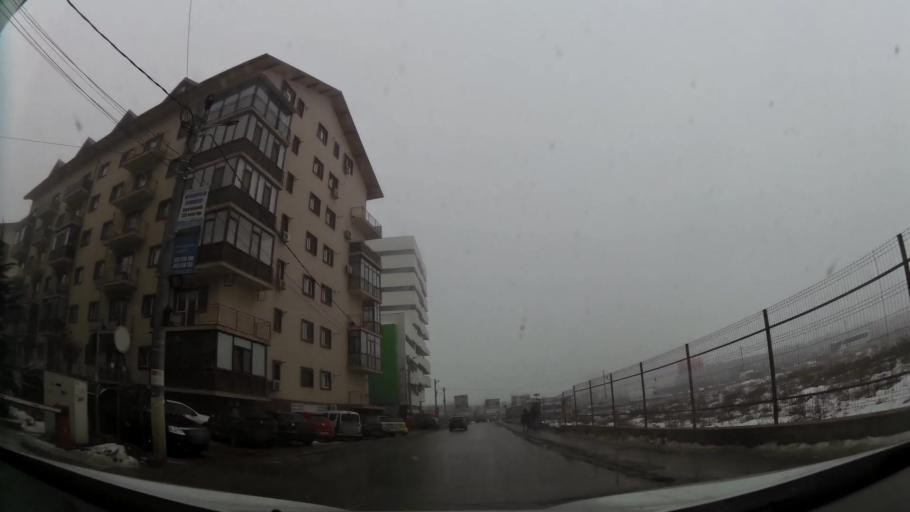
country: RO
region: Ilfov
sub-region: Comuna Chiajna
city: Chiajna
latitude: 44.4423
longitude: 25.9839
